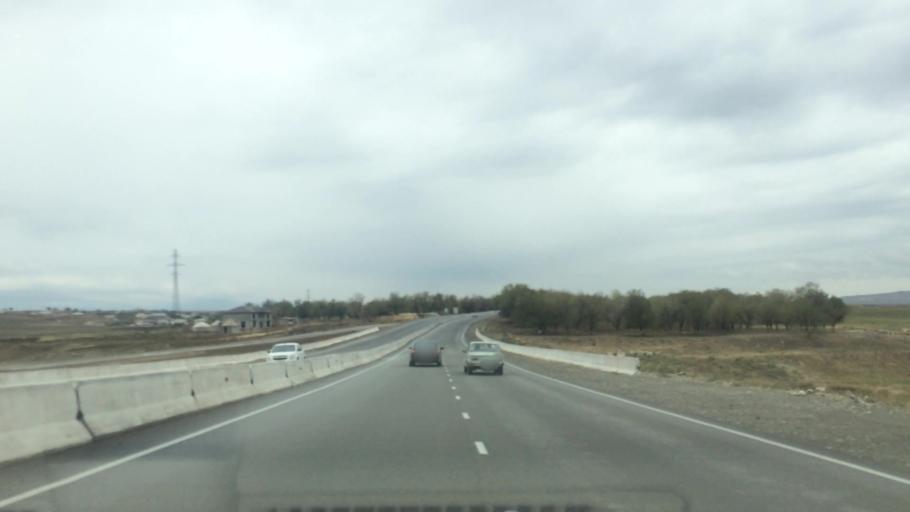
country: UZ
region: Samarqand
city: Bulung'ur
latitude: 39.9208
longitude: 67.5161
